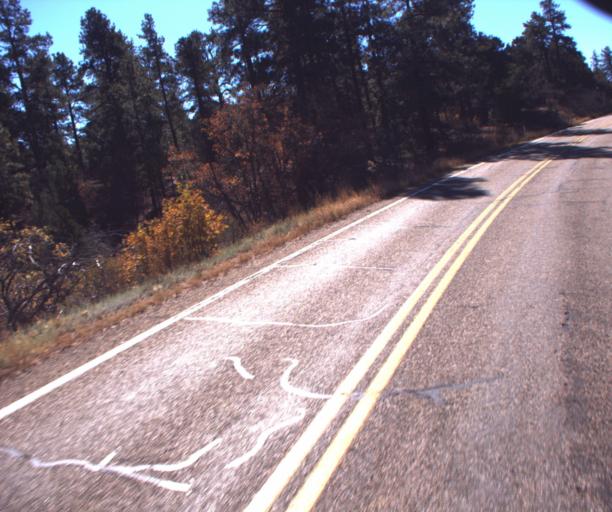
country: US
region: Arizona
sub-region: Coconino County
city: Fredonia
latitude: 36.7837
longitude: -112.2569
